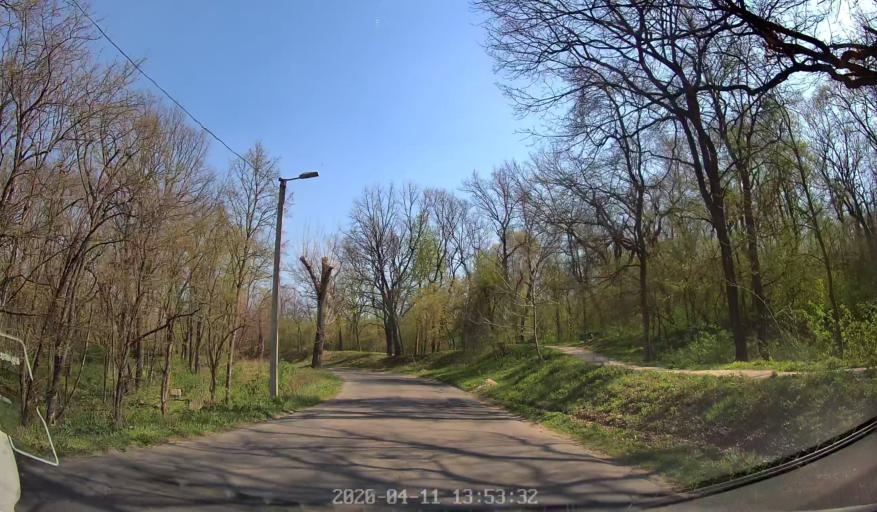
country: MD
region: Chisinau
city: Vadul lui Voda
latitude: 47.0779
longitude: 29.0955
